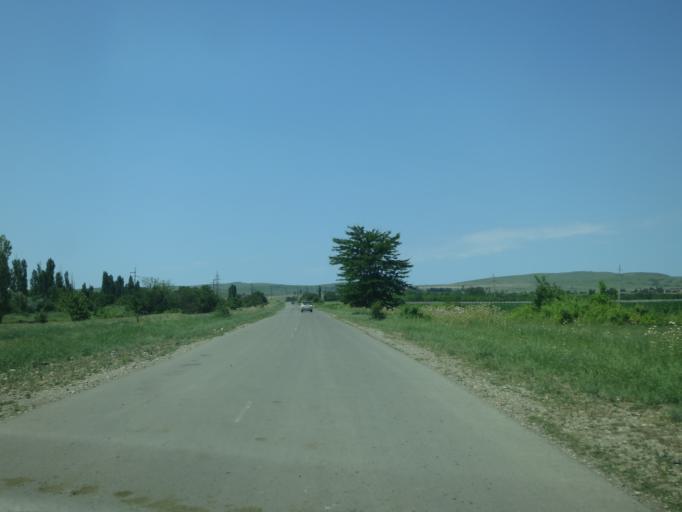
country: GE
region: Kakheti
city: Sagarejo
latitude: 41.6600
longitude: 45.3716
